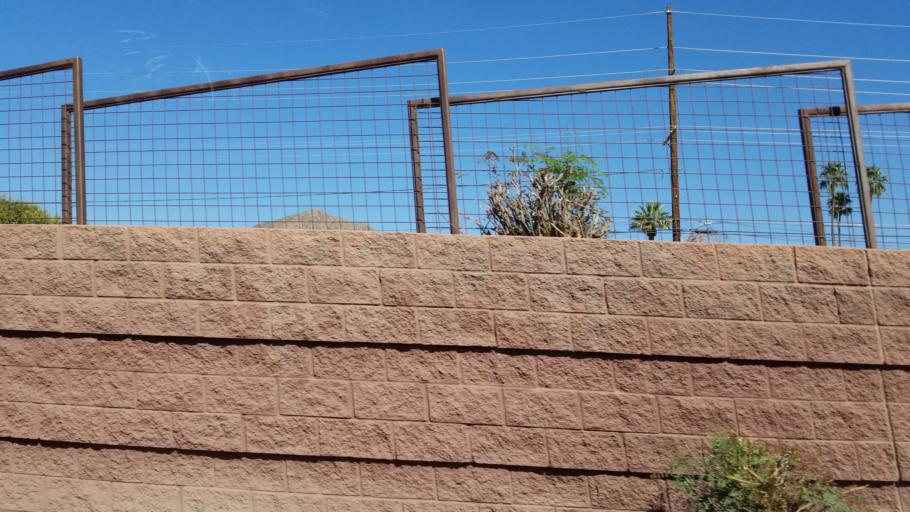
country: US
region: Arizona
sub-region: Maricopa County
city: Paradise Valley
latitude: 33.4908
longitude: -111.9668
